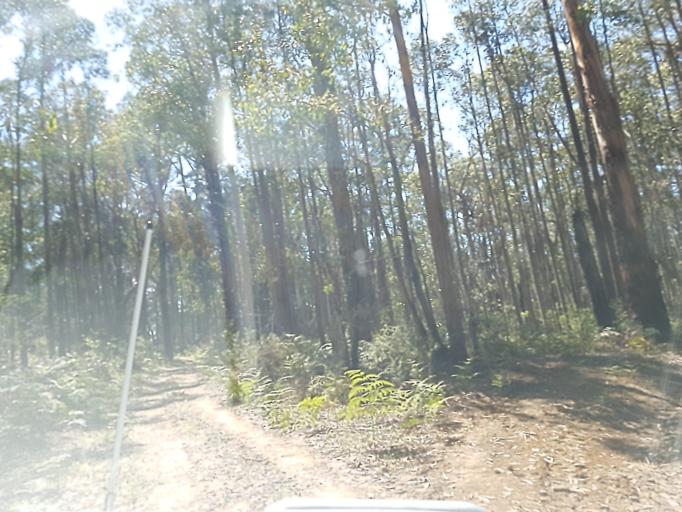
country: AU
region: Victoria
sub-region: East Gippsland
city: Lakes Entrance
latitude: -37.2941
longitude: 148.3271
